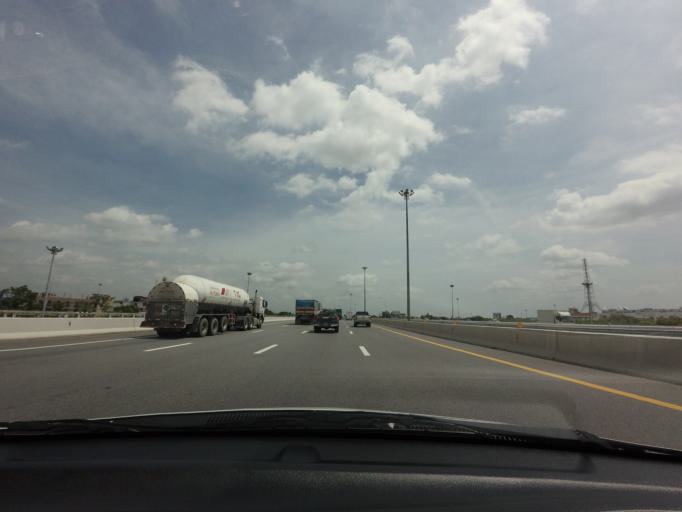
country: TH
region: Bangkok
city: Bueng Kum
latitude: 13.7857
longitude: 100.6847
